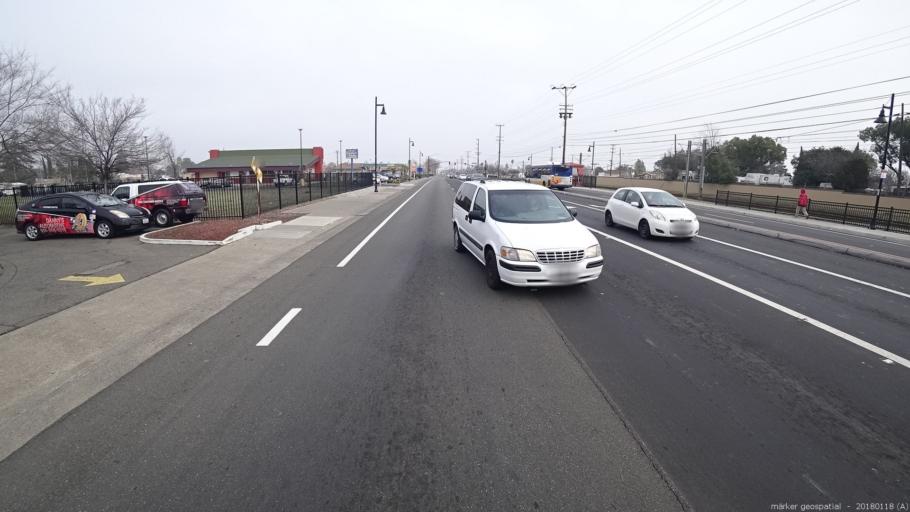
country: US
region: California
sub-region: Sacramento County
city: Rancho Cordova
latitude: 38.5859
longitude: -121.3096
